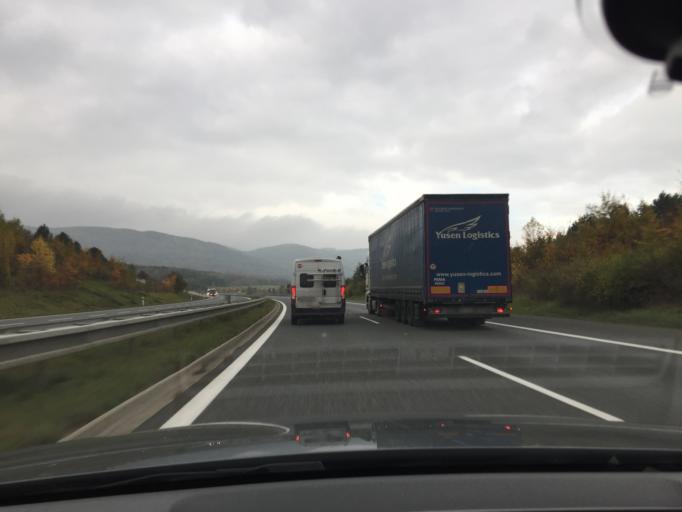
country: CZ
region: Ustecky
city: Chlumec
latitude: 50.6978
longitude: 13.9563
